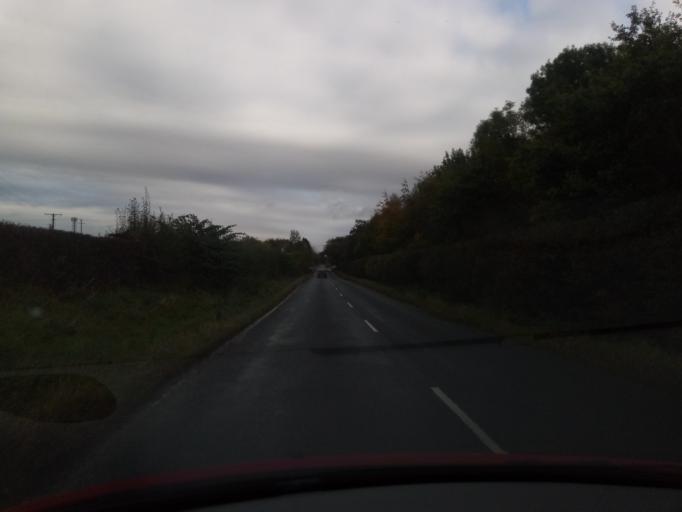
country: GB
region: Scotland
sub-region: The Scottish Borders
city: Saint Boswells
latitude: 55.5671
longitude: -2.6629
